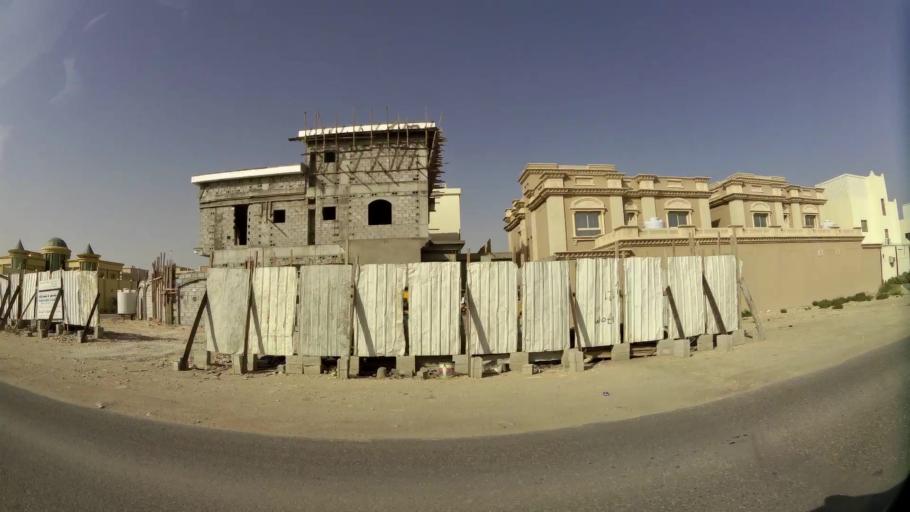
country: QA
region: Baladiyat ar Rayyan
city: Ar Rayyan
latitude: 25.3309
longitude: 51.4231
